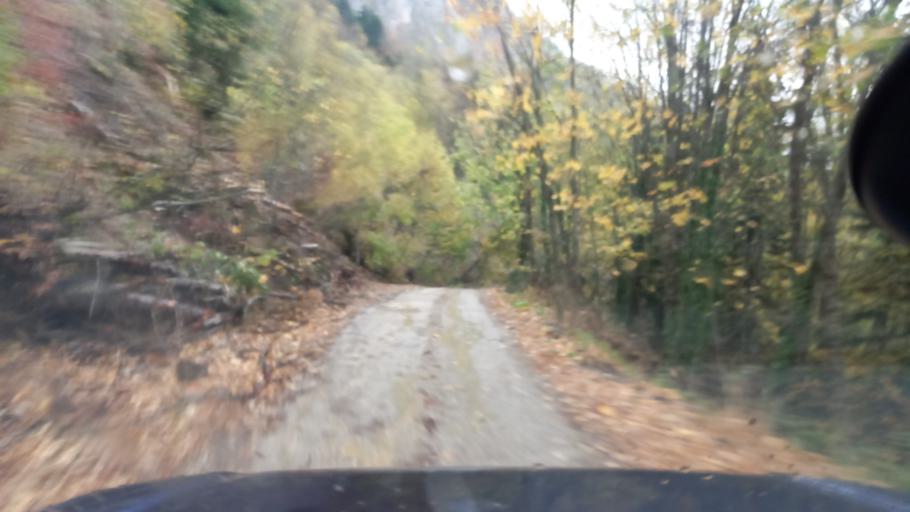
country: RU
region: Krasnodarskiy
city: Neftegorsk
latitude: 44.0479
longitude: 39.8313
